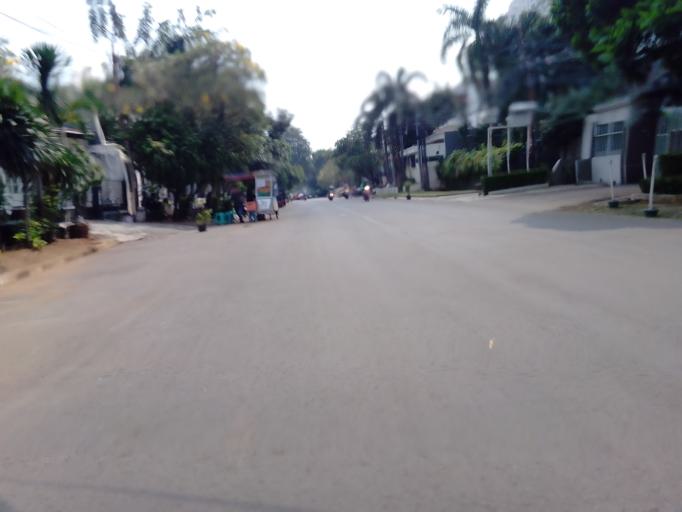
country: ID
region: Jakarta Raya
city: Jakarta
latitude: -6.2255
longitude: 106.7928
